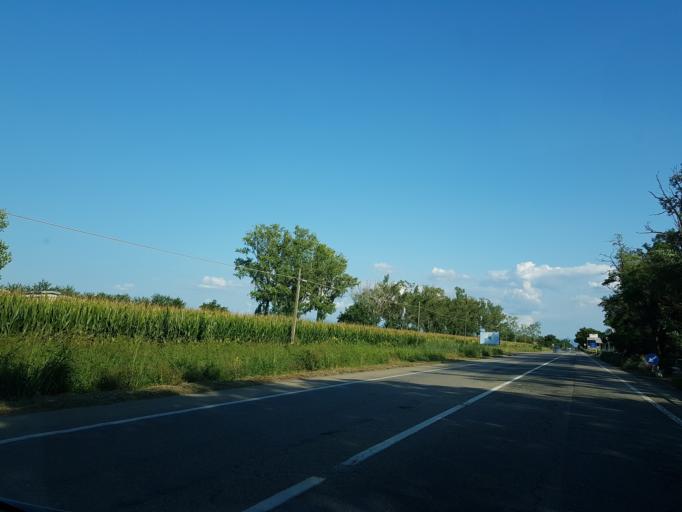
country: IT
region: Piedmont
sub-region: Provincia di Alessandria
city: Litta Parodi-Cascinagrossa
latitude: 44.8553
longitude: 8.7144
